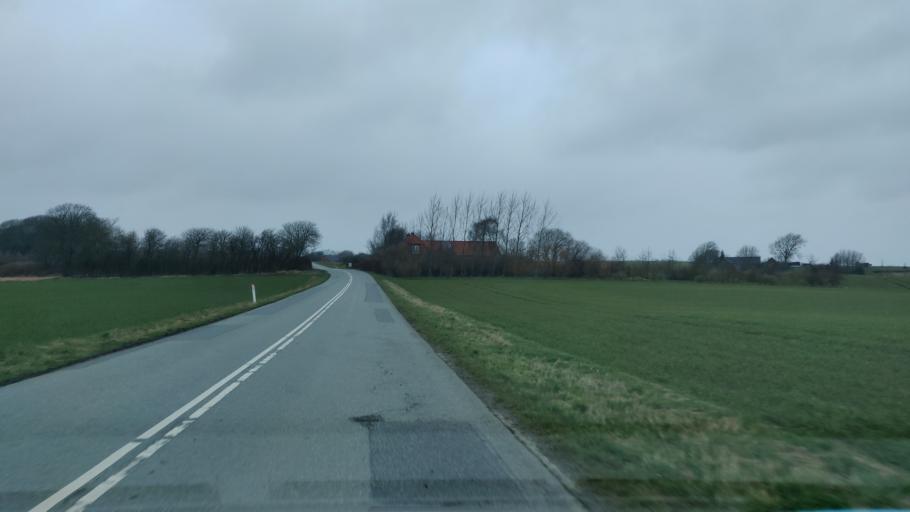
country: DK
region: Central Jutland
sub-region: Skive Kommune
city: Hojslev
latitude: 56.5845
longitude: 9.2256
